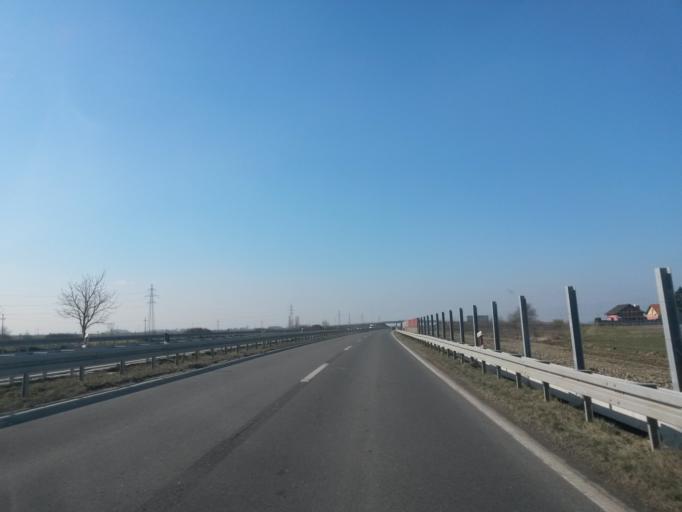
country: HR
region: Osjecko-Baranjska
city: Visnjevac
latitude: 45.5550
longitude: 18.6201
